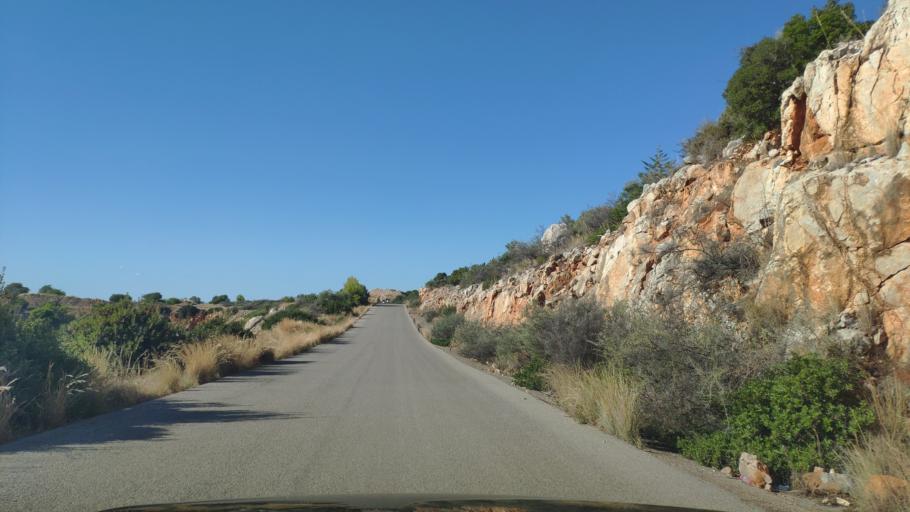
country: GR
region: Attica
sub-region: Nomos Piraios
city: Galatas
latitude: 37.5655
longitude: 23.3619
